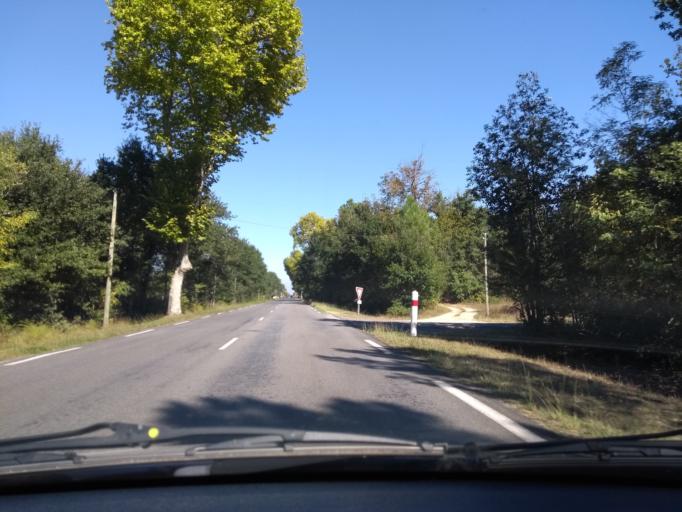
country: FR
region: Aquitaine
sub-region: Departement de la Gironde
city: Le Barp
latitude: 44.5679
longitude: -0.7814
